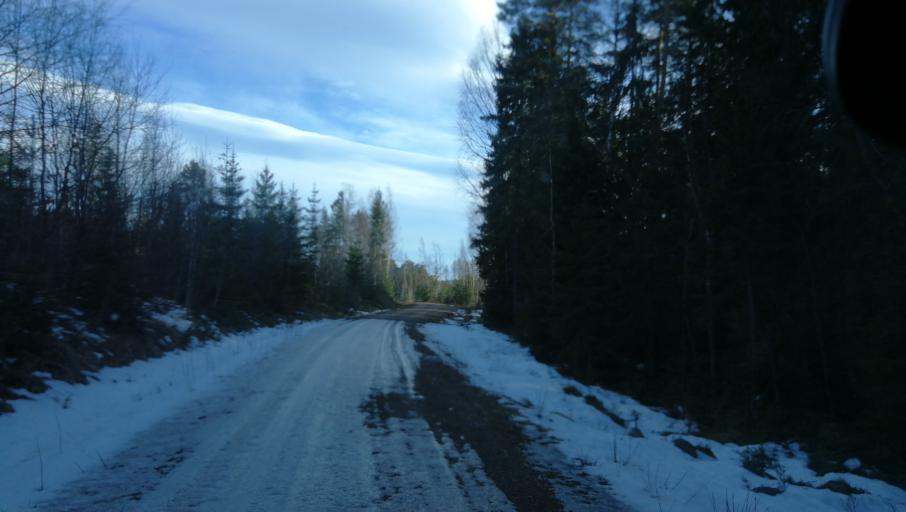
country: SE
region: Dalarna
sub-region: Vansbro Kommun
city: Vansbro
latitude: 60.8025
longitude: 14.2120
